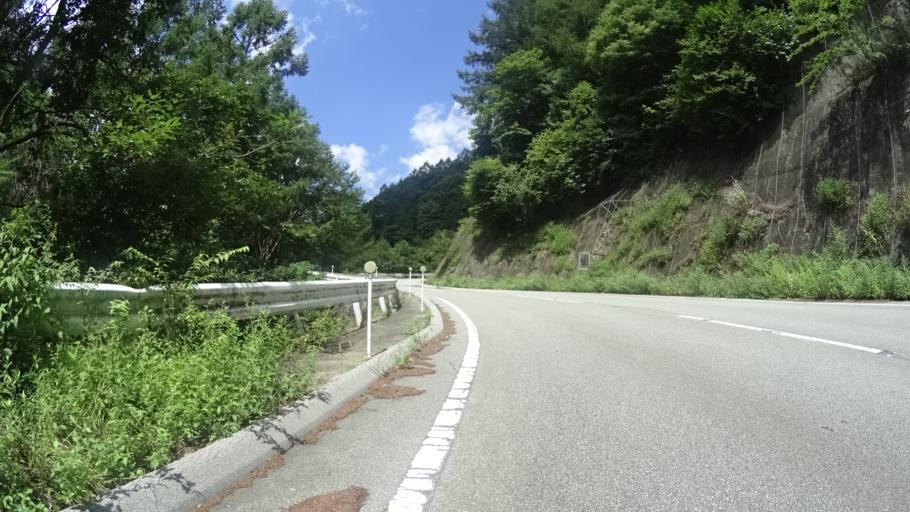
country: JP
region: Yamanashi
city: Enzan
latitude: 35.7976
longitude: 138.6766
